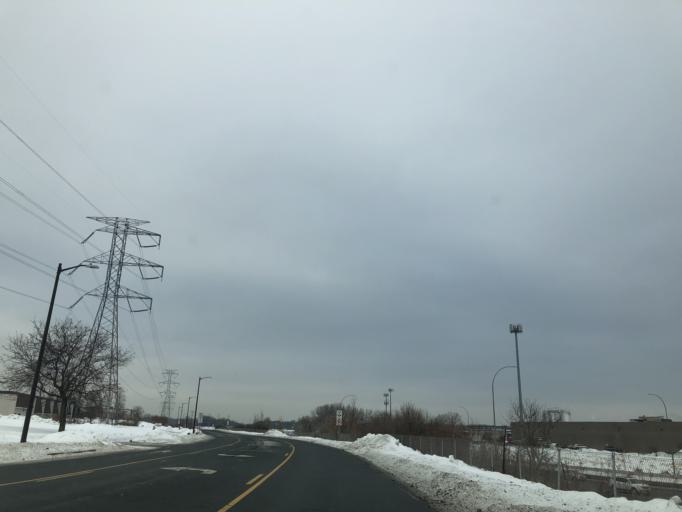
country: US
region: Minnesota
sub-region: Ramsey County
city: New Brighton
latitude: 45.0767
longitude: -93.1845
